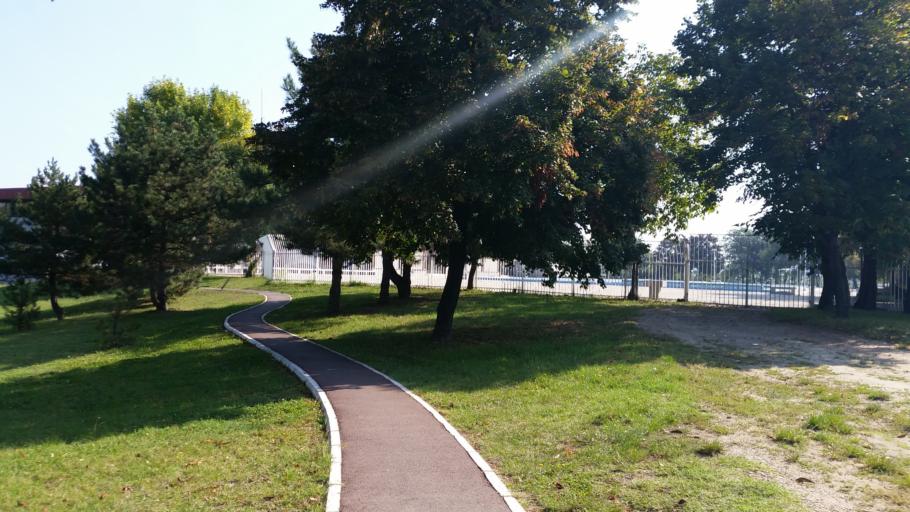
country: RS
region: Central Serbia
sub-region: Belgrade
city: Zemun
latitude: 44.8255
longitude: 20.3927
